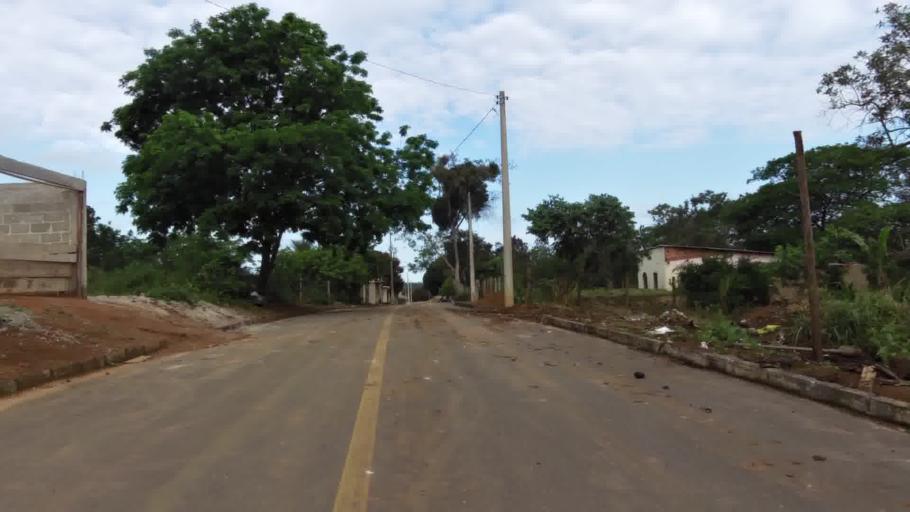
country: BR
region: Espirito Santo
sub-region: Piuma
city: Piuma
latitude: -20.7926
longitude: -40.6426
